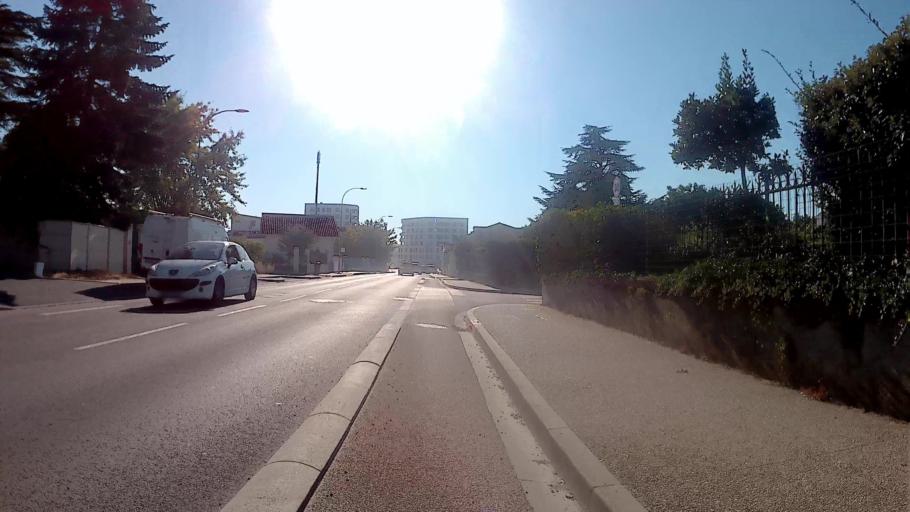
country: FR
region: Aquitaine
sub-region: Departement de la Gironde
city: Villenave-d'Ornon
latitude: 44.7816
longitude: -0.5644
